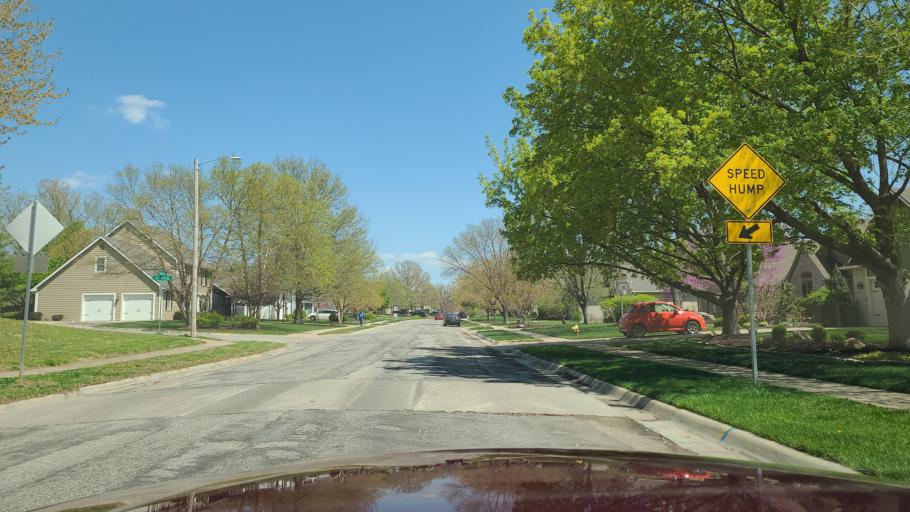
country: US
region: Kansas
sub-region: Douglas County
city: Lawrence
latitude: 38.9675
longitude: -95.3010
